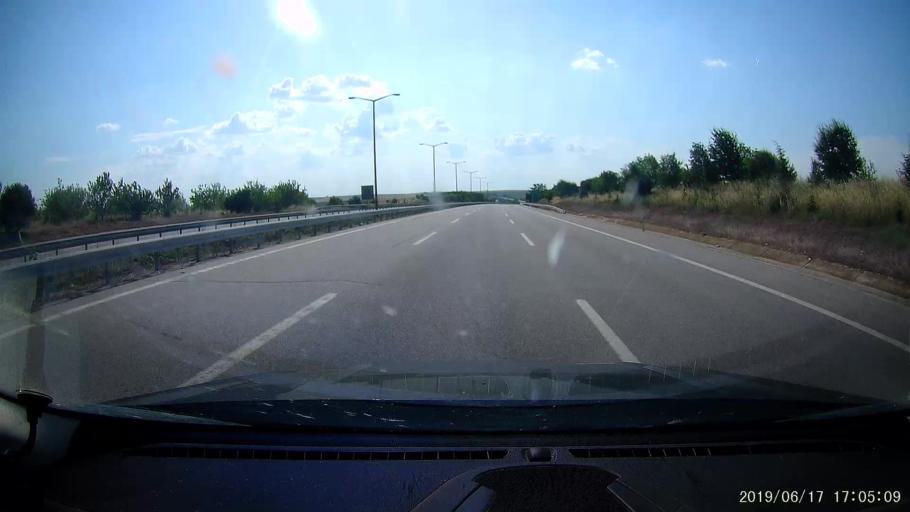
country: TR
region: Edirne
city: Haskoy
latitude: 41.6580
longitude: 26.7073
